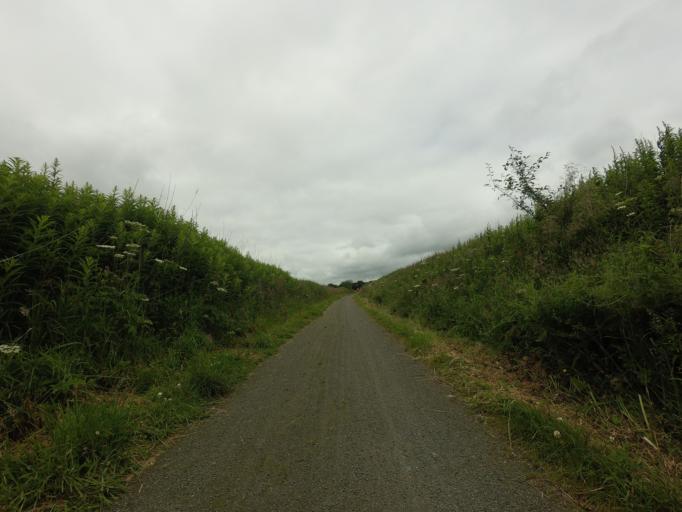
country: GB
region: Scotland
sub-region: Aberdeenshire
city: Ellon
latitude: 57.4844
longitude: -2.1350
